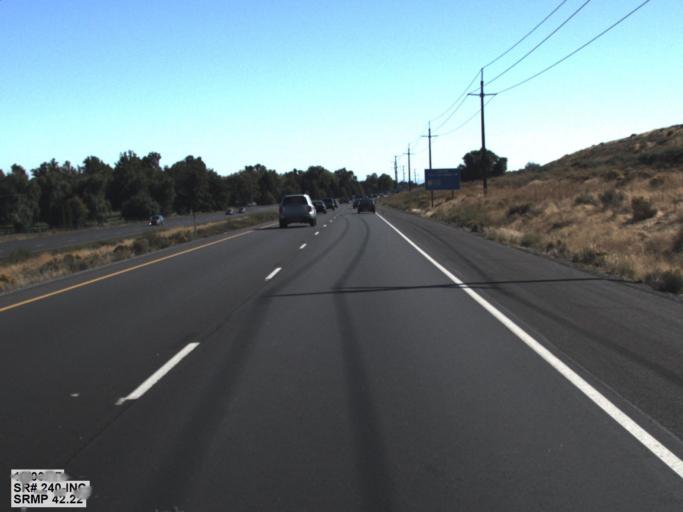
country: US
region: Washington
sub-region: Benton County
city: Kennewick
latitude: 46.2211
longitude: -119.1567
